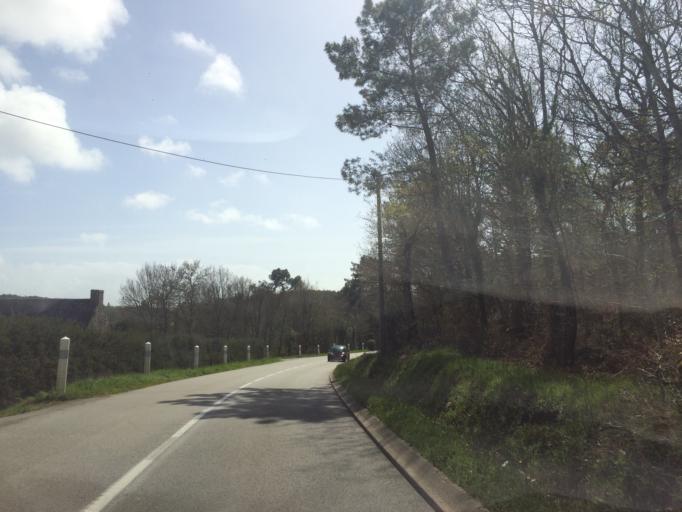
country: FR
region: Brittany
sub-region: Departement du Morbihan
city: Ploemel
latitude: 47.6334
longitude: -3.0475
